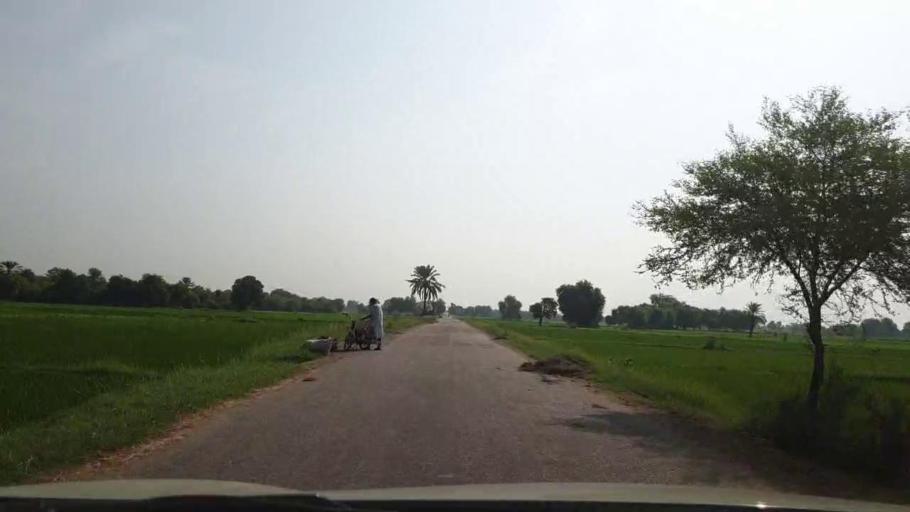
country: PK
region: Sindh
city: Larkana
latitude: 27.4619
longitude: 68.2204
